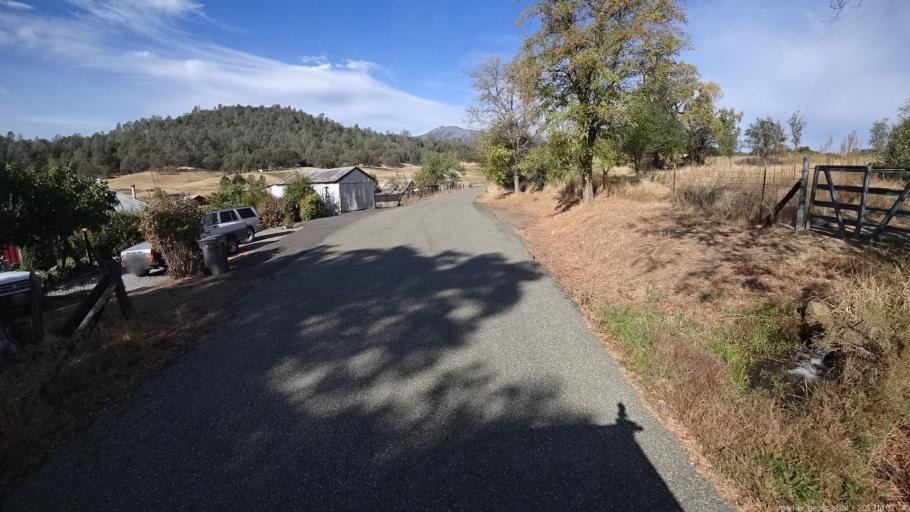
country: US
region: California
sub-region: Shasta County
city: Shasta
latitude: 40.5080
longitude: -122.5473
